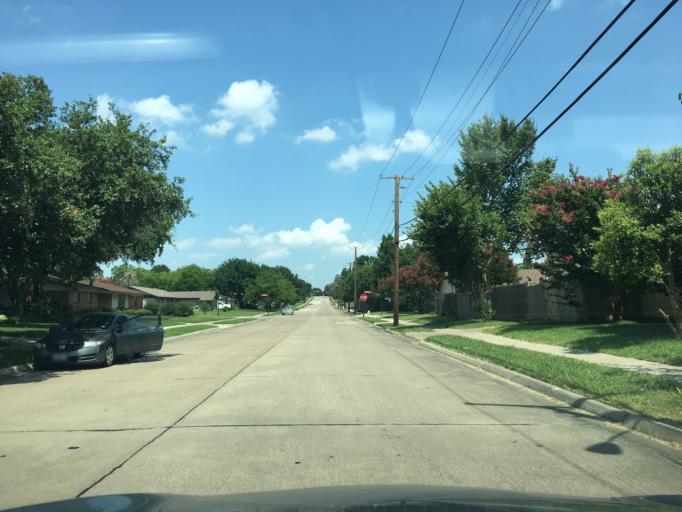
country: US
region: Texas
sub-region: Dallas County
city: Farmers Branch
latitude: 32.9193
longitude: -96.8627
